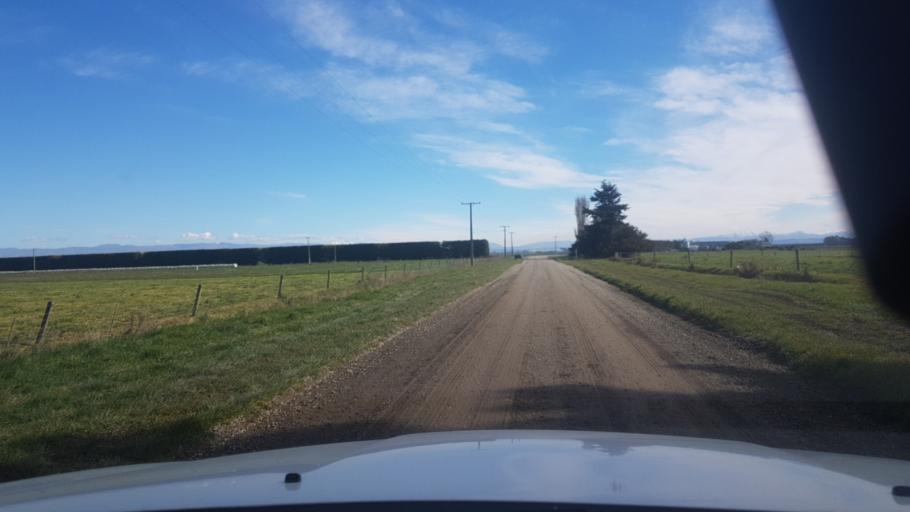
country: NZ
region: Canterbury
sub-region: Timaru District
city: Timaru
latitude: -44.2458
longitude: 171.3713
